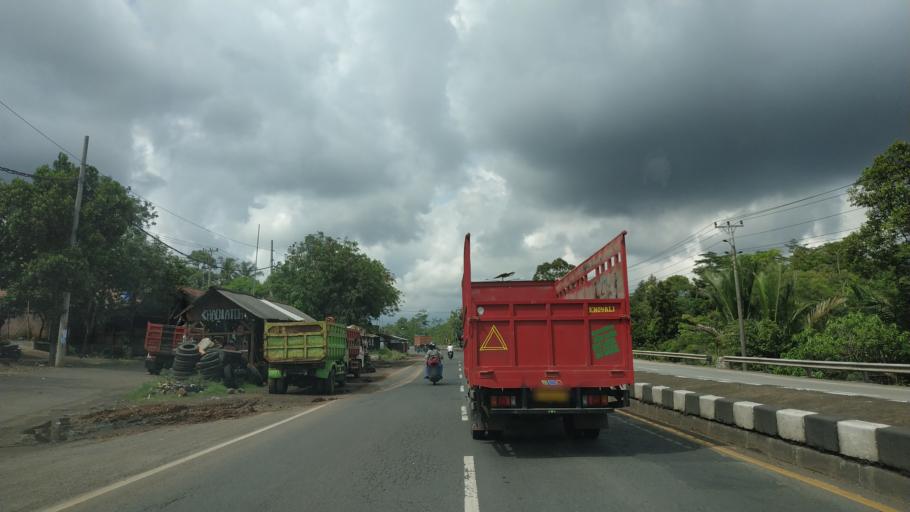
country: ID
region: Central Java
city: Pekalongan
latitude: -6.9379
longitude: 109.7747
